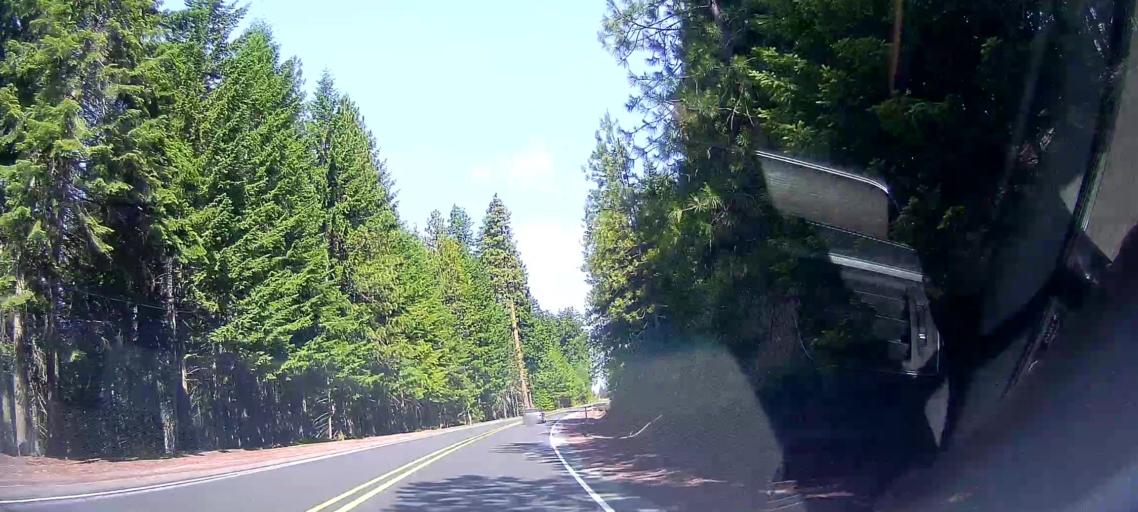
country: US
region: Oregon
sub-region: Clackamas County
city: Mount Hood Village
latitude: 45.1271
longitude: -121.5947
